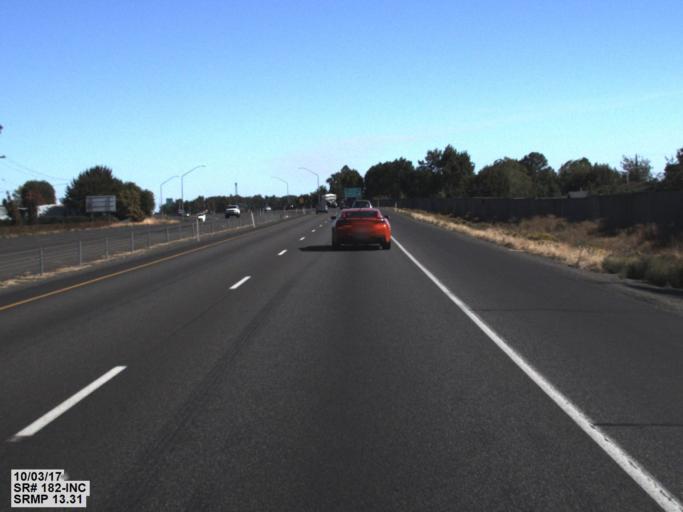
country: US
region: Washington
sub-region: Franklin County
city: Pasco
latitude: 46.2484
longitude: -119.1042
